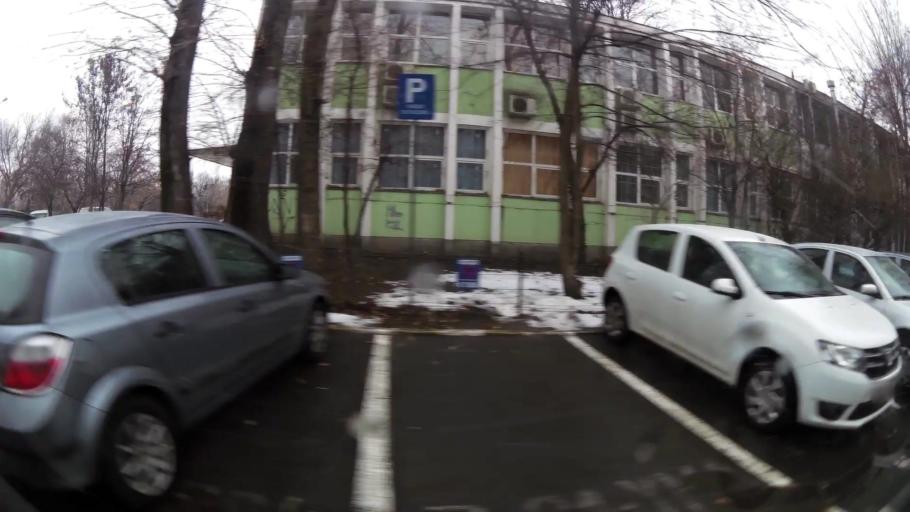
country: RO
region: Ilfov
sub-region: Comuna Chiajna
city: Rosu
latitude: 44.4834
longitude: 26.0509
